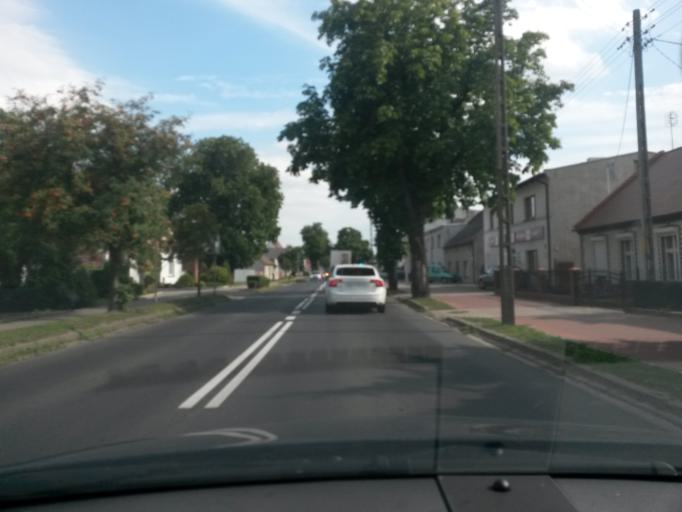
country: PL
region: Greater Poland Voivodeship
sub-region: Powiat gostynski
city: Gostyn
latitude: 51.8880
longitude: 17.0096
